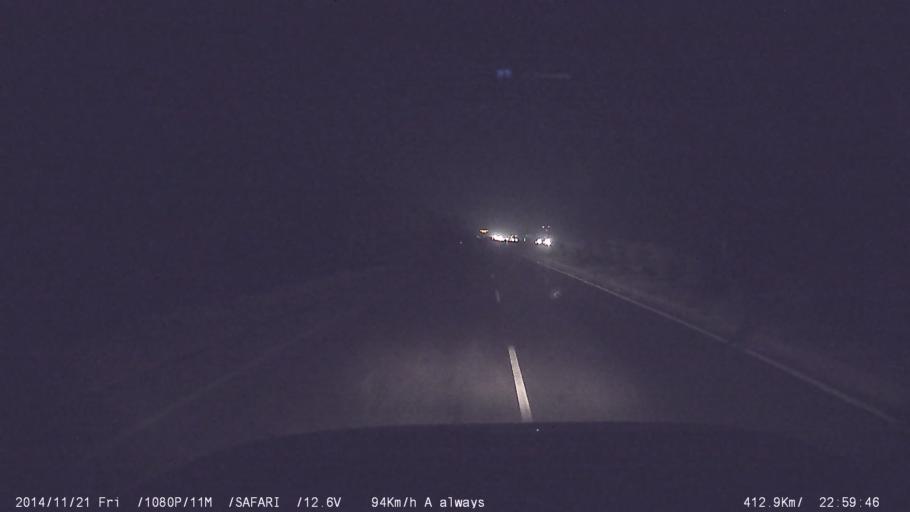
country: IN
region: Tamil Nadu
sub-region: Villupuram
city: Vikravandi
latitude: 12.0718
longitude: 79.5500
